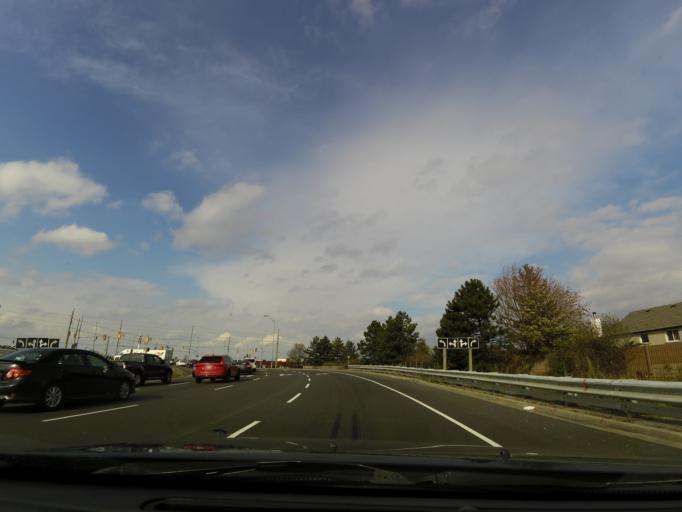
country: CA
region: Ontario
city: Brampton
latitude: 43.7256
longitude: -79.7629
